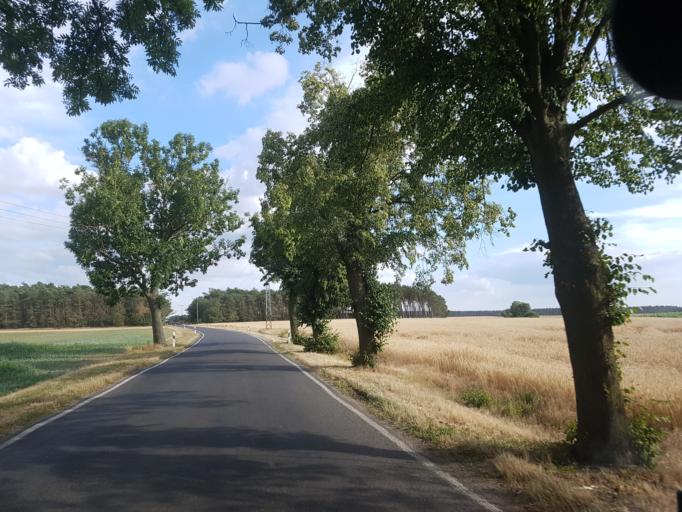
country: DE
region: Brandenburg
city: Herzberg
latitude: 51.7586
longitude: 13.2678
